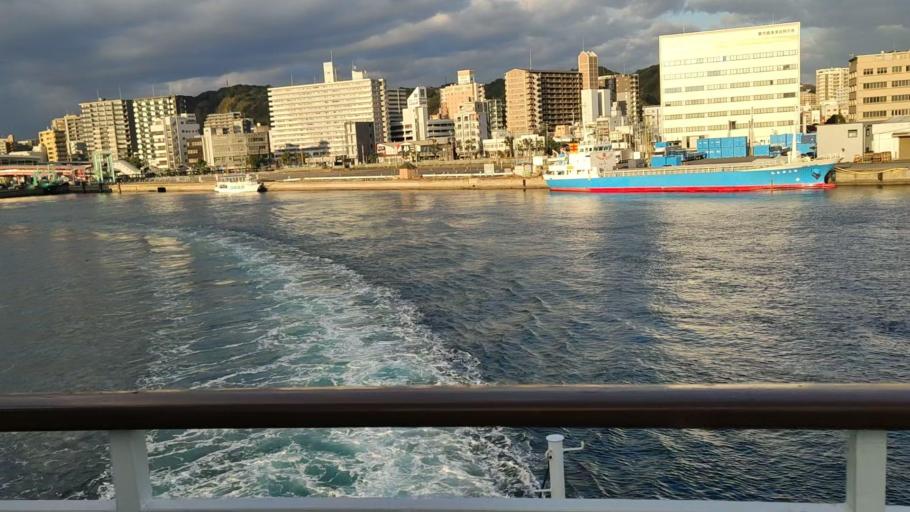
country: JP
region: Kagoshima
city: Kagoshima-shi
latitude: 31.5982
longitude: 130.5669
